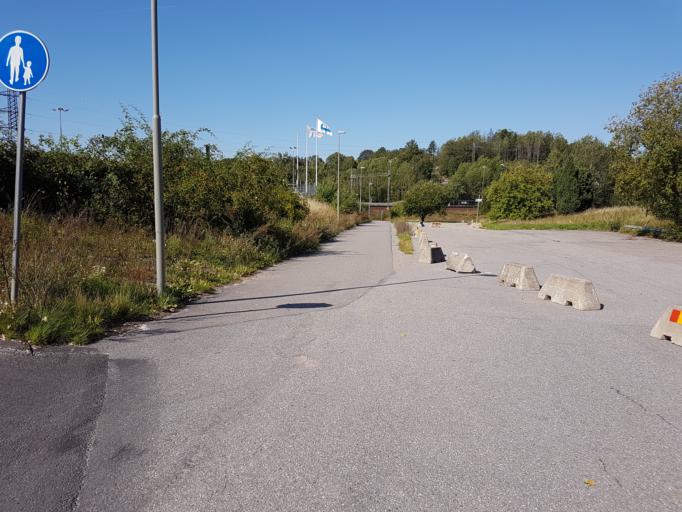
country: SE
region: Stockholm
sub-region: Huddinge Kommun
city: Huddinge
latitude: 59.2230
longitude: 17.9557
